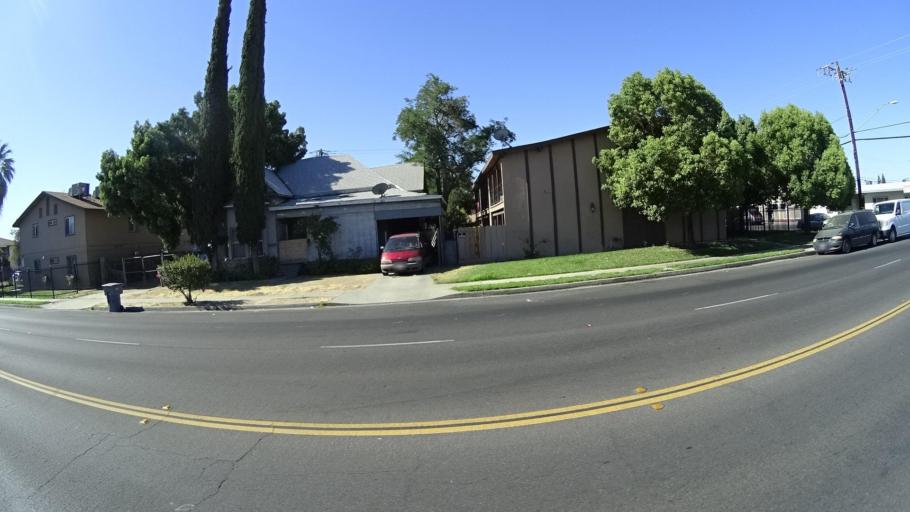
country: US
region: California
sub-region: Fresno County
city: Fresno
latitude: 36.7578
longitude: -119.7699
